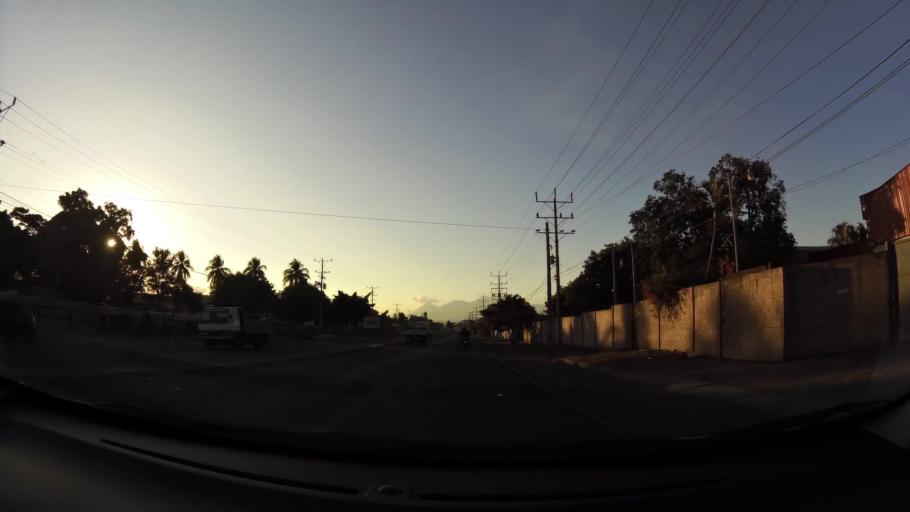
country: SV
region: Sonsonate
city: Armenia
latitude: 13.7364
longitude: -89.3961
